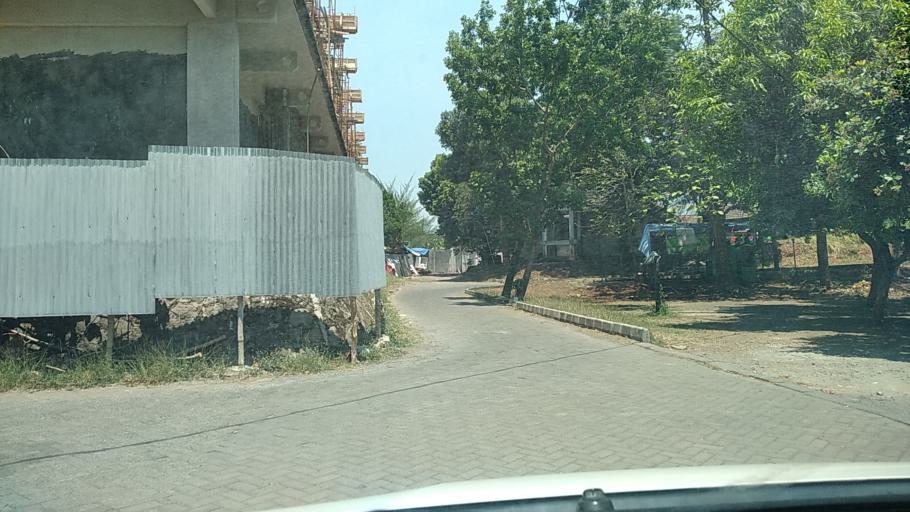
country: ID
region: Central Java
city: Semarang
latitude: -7.0494
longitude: 110.4000
